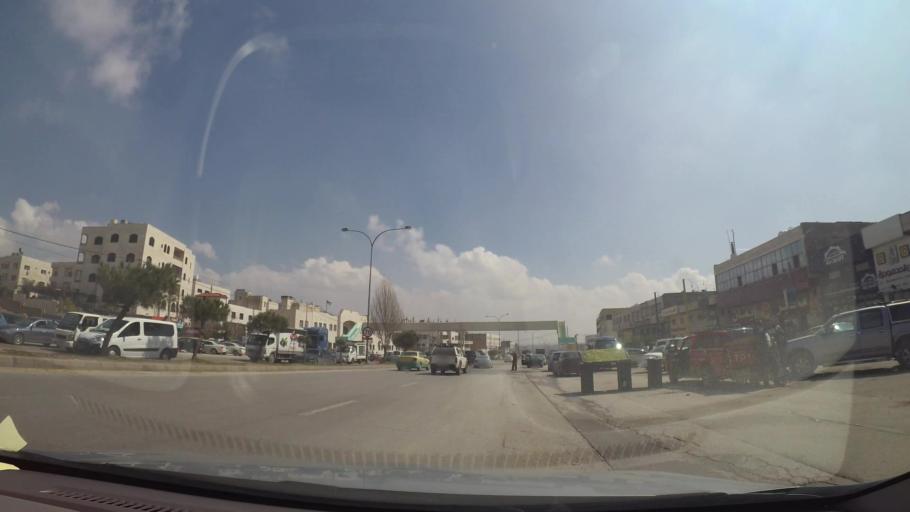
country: JO
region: Amman
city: Al Bunayyat ash Shamaliyah
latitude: 31.9014
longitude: 35.8929
